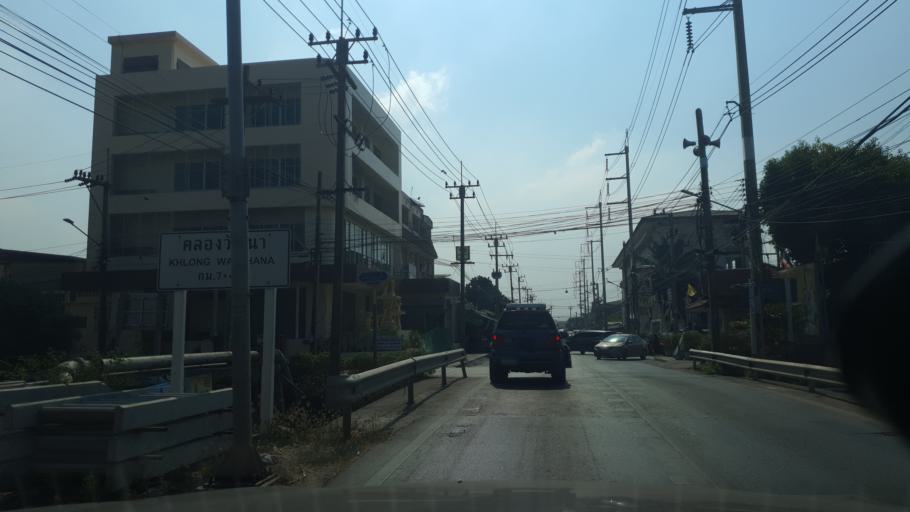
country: TH
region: Nakhon Pathom
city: Salaya
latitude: 13.7727
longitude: 100.2851
